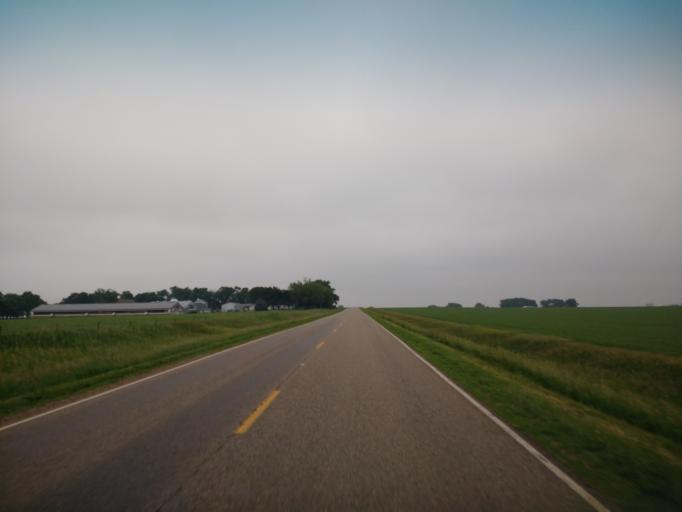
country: US
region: Iowa
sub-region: Sioux County
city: Alton
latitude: 42.9885
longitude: -95.8993
